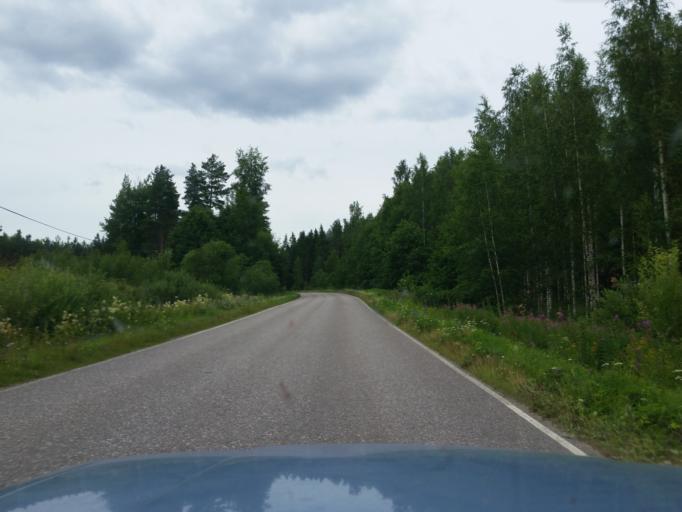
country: FI
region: Uusimaa
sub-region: Helsinki
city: Sammatti
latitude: 60.4196
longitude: 23.8260
